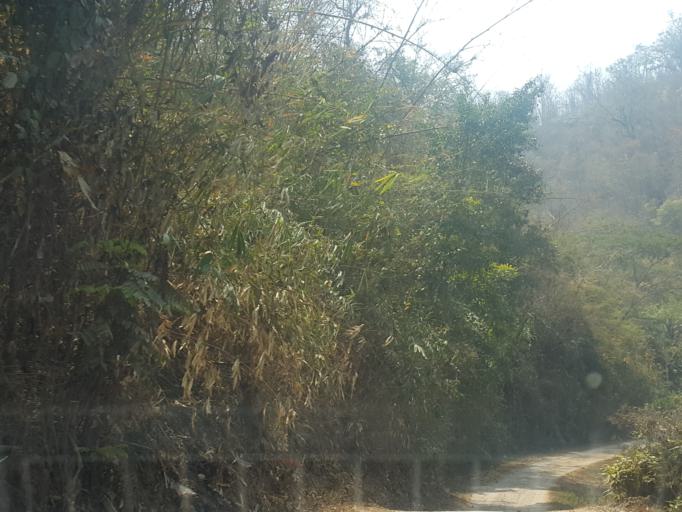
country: TH
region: Chiang Mai
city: Hang Dong
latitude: 18.7345
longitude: 98.8289
